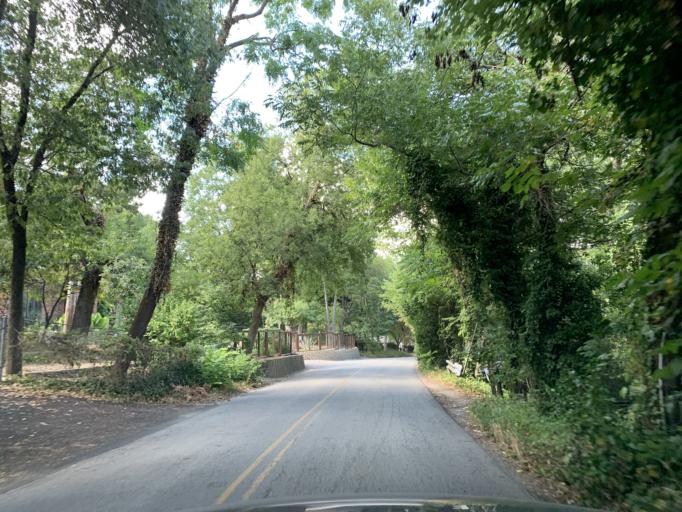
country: US
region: Texas
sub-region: Dallas County
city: Cockrell Hill
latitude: 32.7430
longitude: -96.8702
